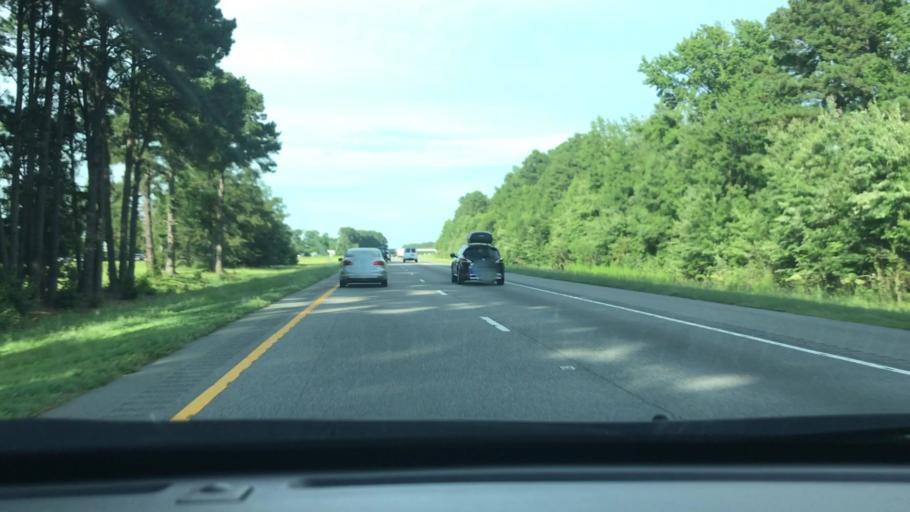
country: US
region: North Carolina
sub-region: Robeson County
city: Fairmont
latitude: 34.5840
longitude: -79.1352
